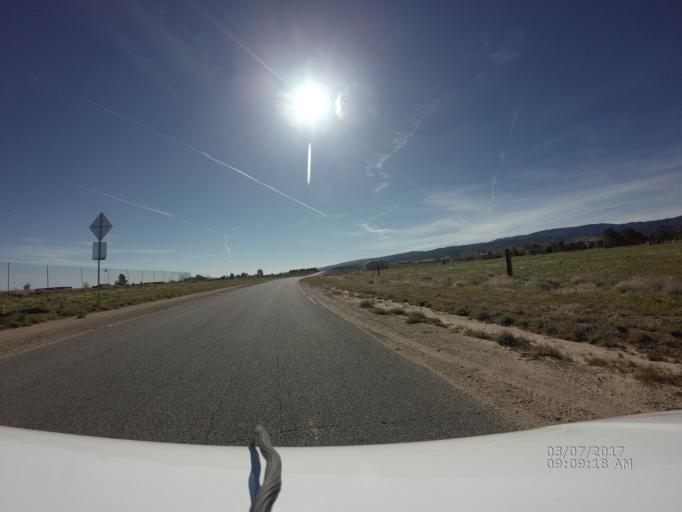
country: US
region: California
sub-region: Los Angeles County
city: Green Valley
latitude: 34.7813
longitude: -118.5840
